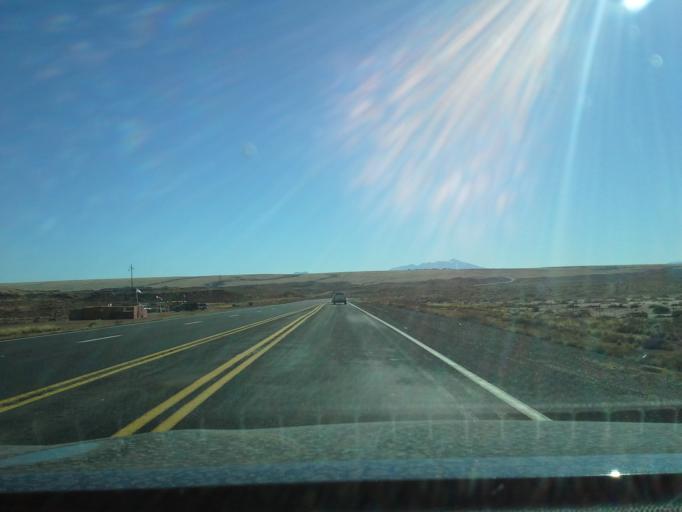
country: US
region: Arizona
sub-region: Coconino County
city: Tuba City
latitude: 35.7961
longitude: -111.4480
